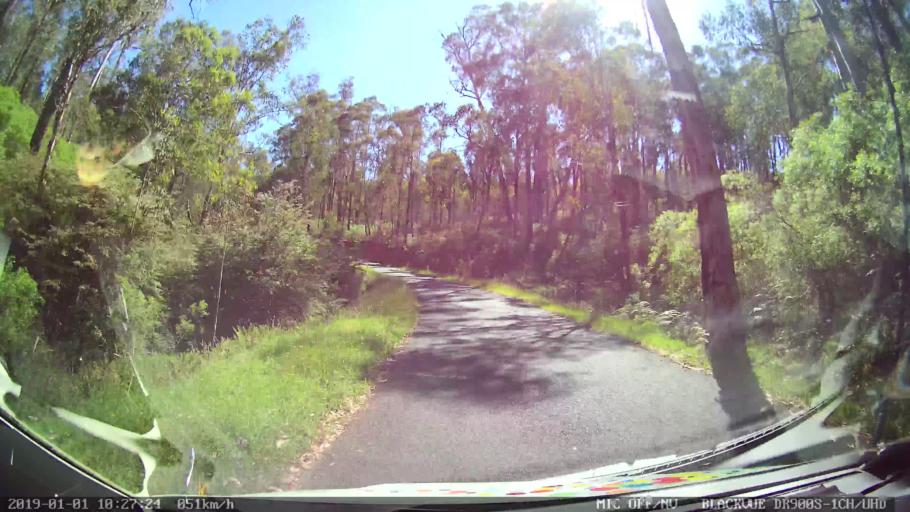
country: AU
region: New South Wales
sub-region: Snowy River
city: Jindabyne
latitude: -36.0664
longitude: 148.2367
